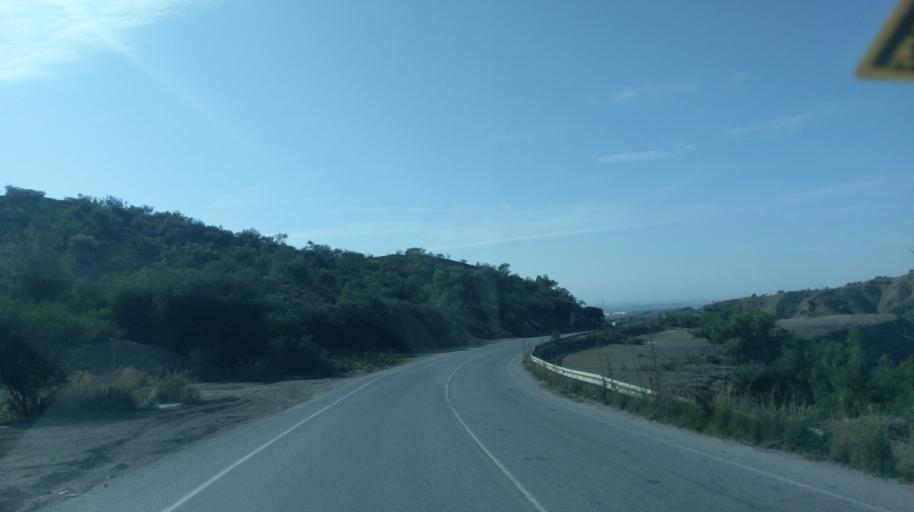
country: CY
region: Lefkosia
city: Nicosia
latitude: 35.2497
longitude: 33.4616
